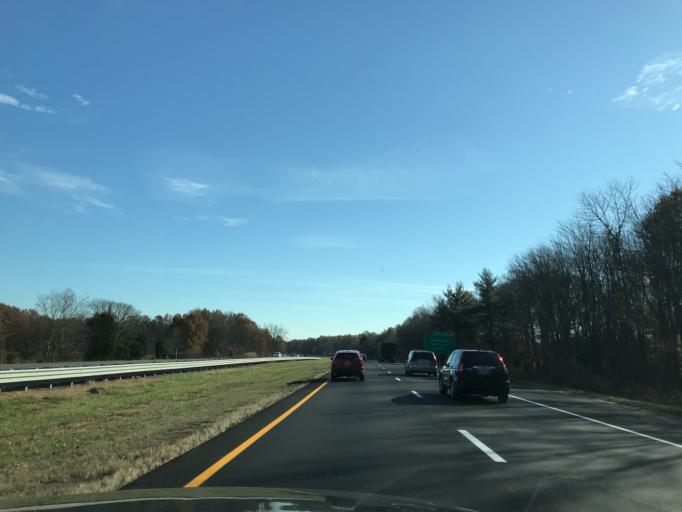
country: US
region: New Jersey
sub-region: Morris County
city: East Hanover
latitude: 40.8369
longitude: -74.3369
